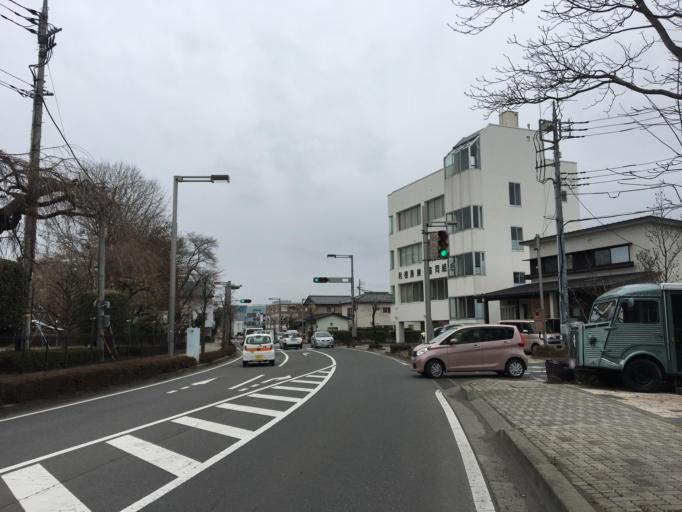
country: JP
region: Gunma
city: Numata
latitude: 36.6465
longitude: 139.0414
